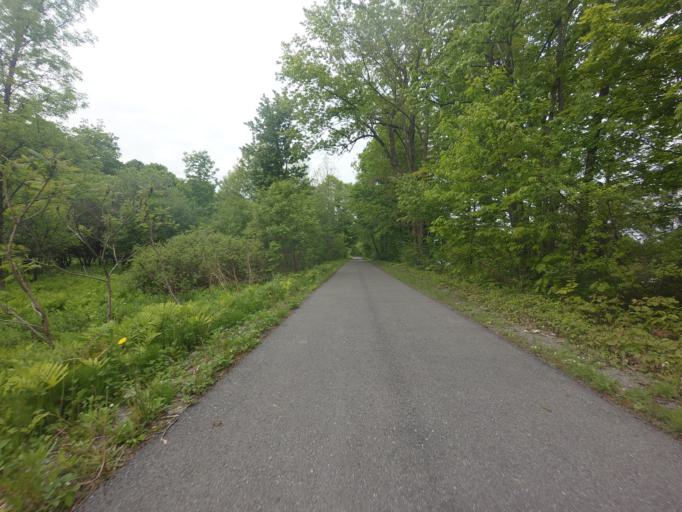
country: US
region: New York
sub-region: Jefferson County
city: Calcium
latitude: 43.9874
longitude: -75.8387
